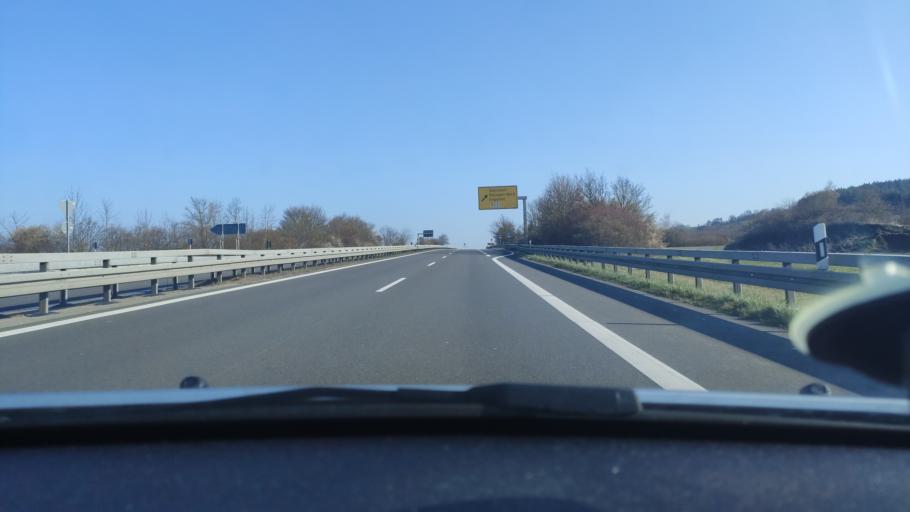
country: DE
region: Baden-Wuerttemberg
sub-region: Tuebingen Region
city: Balingen
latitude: 48.2826
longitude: 8.8600
